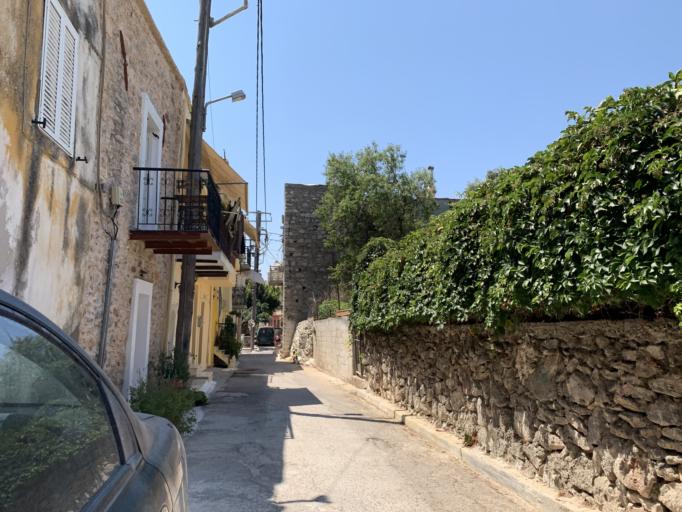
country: GR
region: North Aegean
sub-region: Chios
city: Thymiana
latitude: 38.2275
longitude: 25.9971
